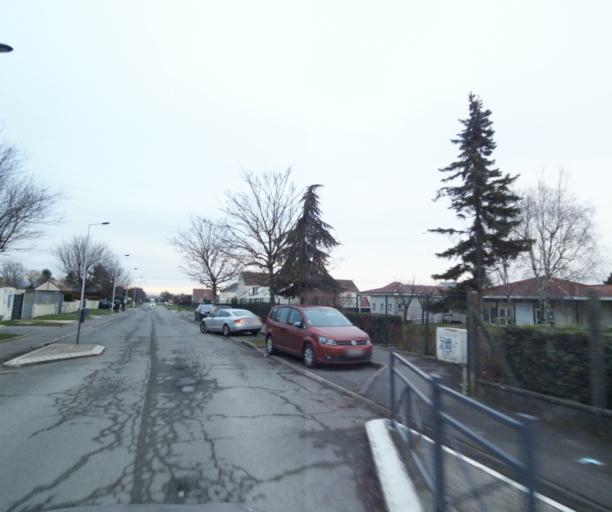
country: FR
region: Ile-de-France
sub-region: Departement de Seine-et-Marne
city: Dammartin-en-Goele
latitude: 49.0630
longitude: 2.6876
